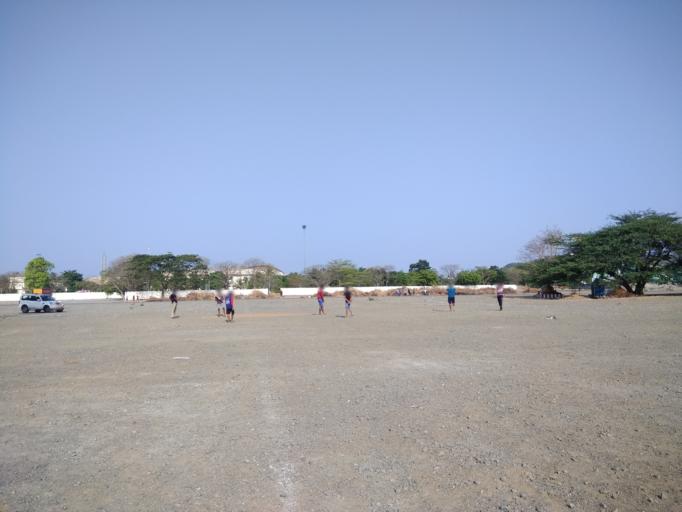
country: IN
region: Tamil Nadu
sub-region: Kancheepuram
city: Saint Thomas Mount
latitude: 13.0136
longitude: 80.1872
